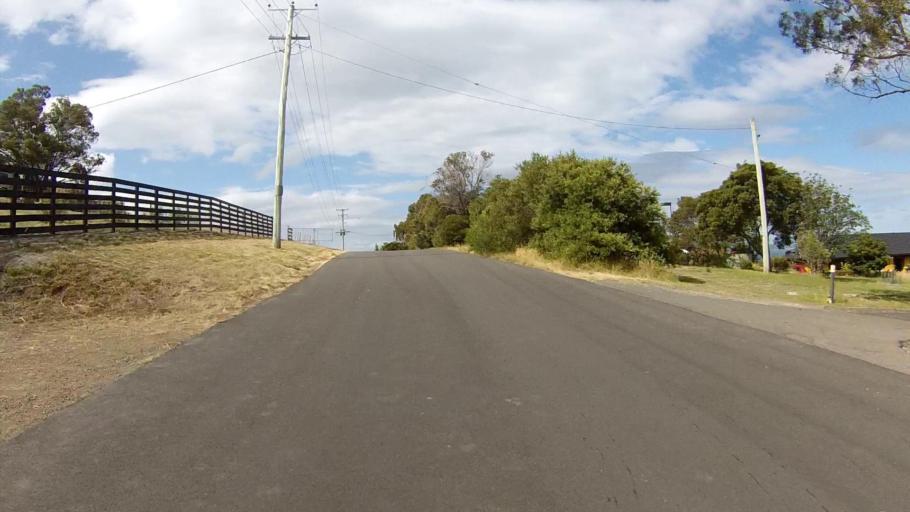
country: AU
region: Tasmania
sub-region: Clarence
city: Acton Park
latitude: -42.8846
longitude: 147.5021
